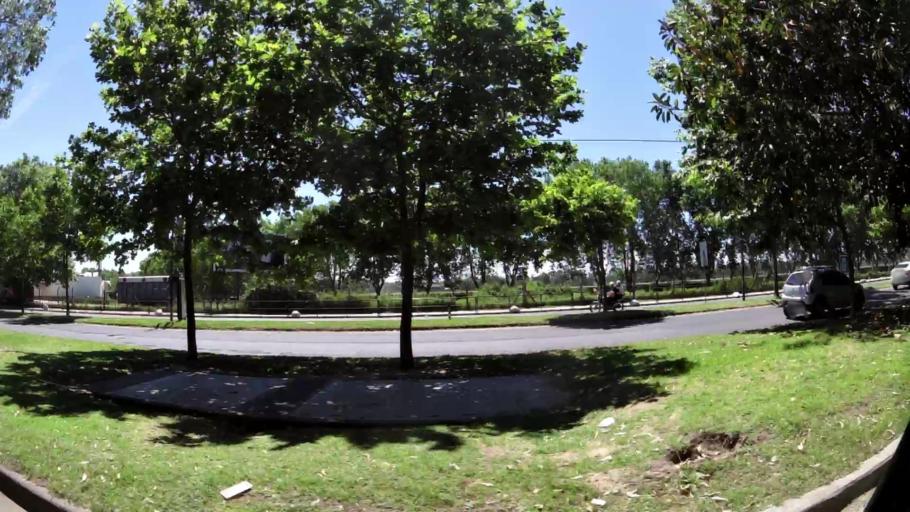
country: AR
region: Buenos Aires
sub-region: Partido de San Isidro
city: San Isidro
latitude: -34.4979
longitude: -58.5404
